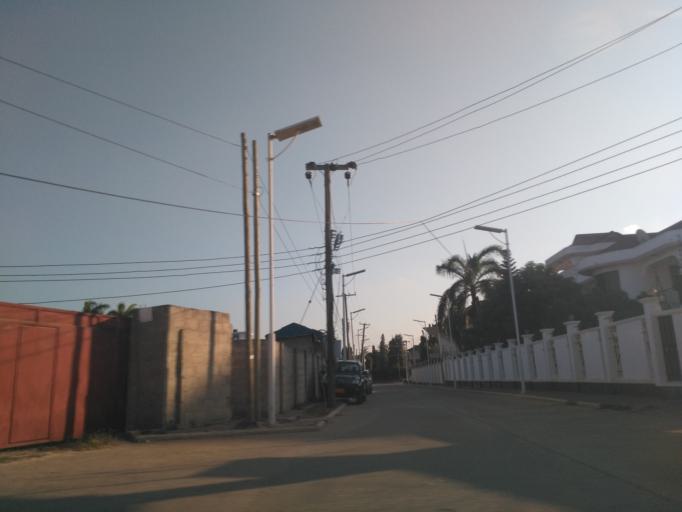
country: TZ
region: Dar es Salaam
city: Magomeni
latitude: -6.7618
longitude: 39.2559
